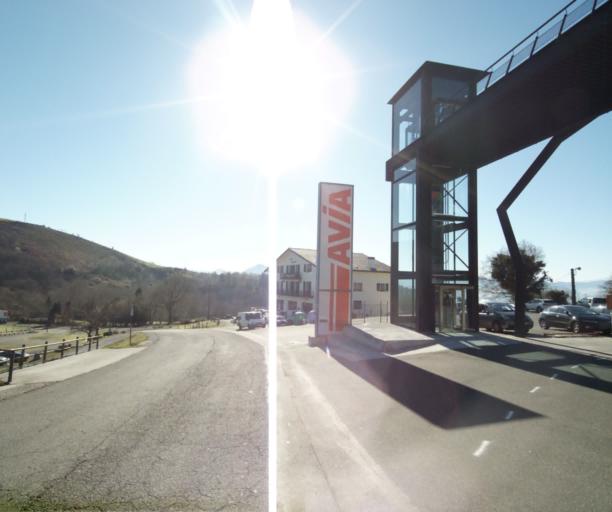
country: ES
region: Navarre
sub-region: Provincia de Navarra
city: Bera
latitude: 43.3097
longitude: -1.6871
